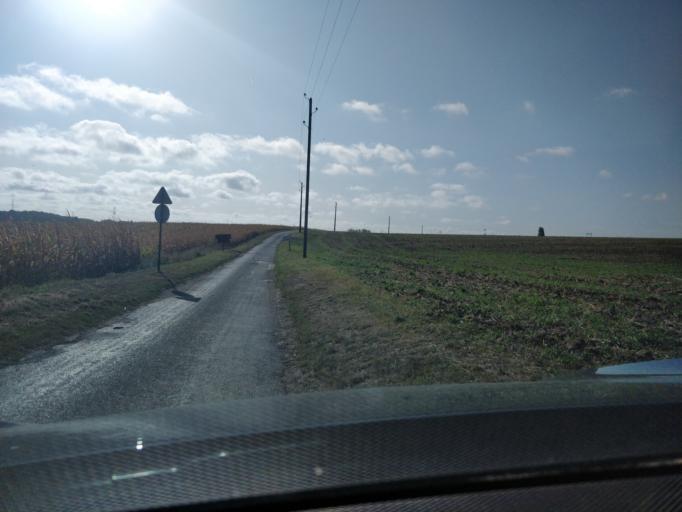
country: FR
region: Ile-de-France
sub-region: Departement de l'Essonne
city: Forges-les-Bains
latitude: 48.6227
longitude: 2.1037
